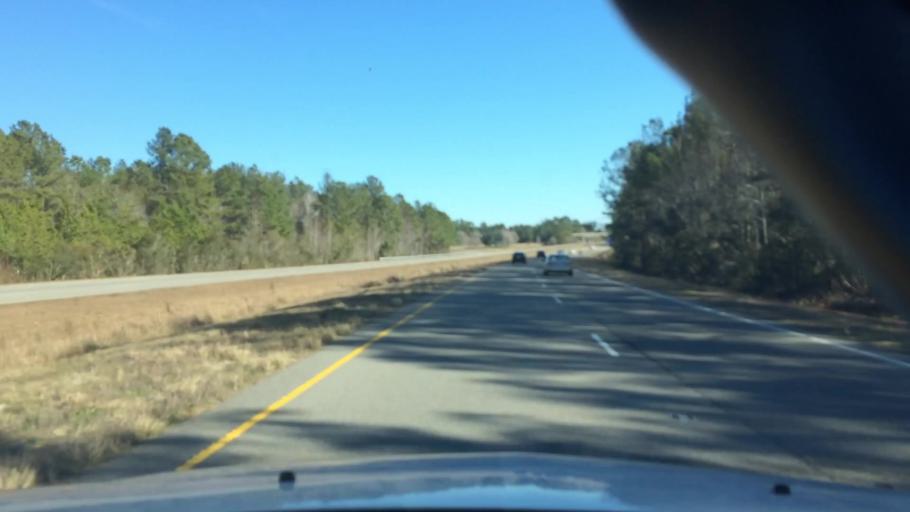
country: US
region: North Carolina
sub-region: Brunswick County
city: Shallotte
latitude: 33.9718
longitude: -78.4101
